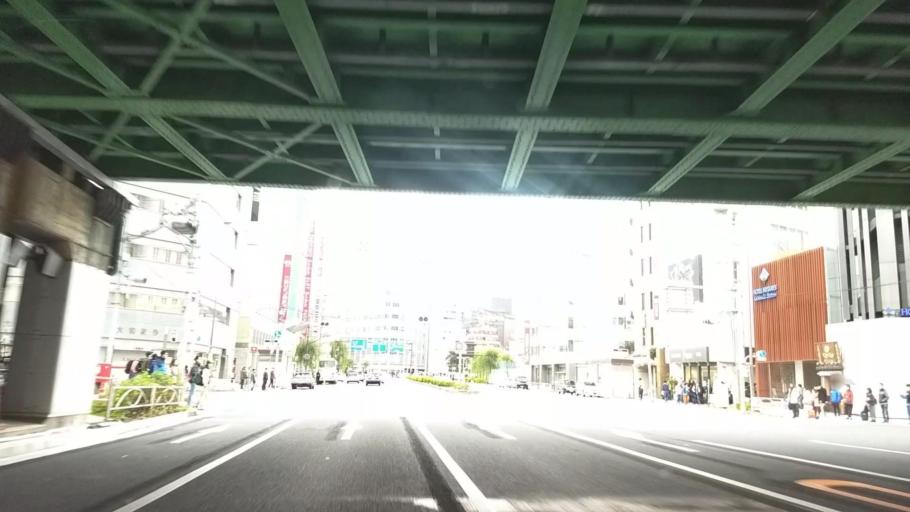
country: JP
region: Tokyo
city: Tokyo
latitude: 35.6265
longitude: 139.7234
